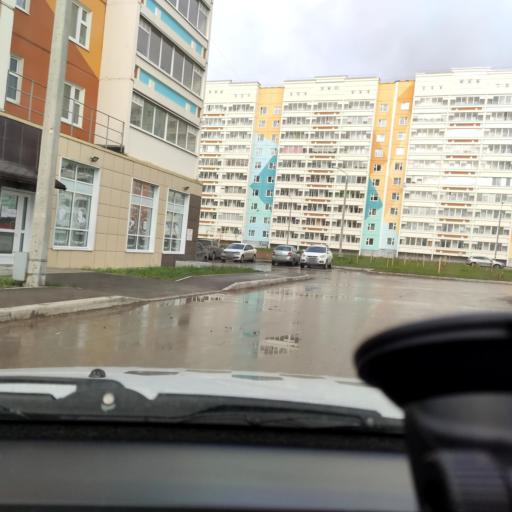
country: RU
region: Perm
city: Perm
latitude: 58.0499
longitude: 56.3489
